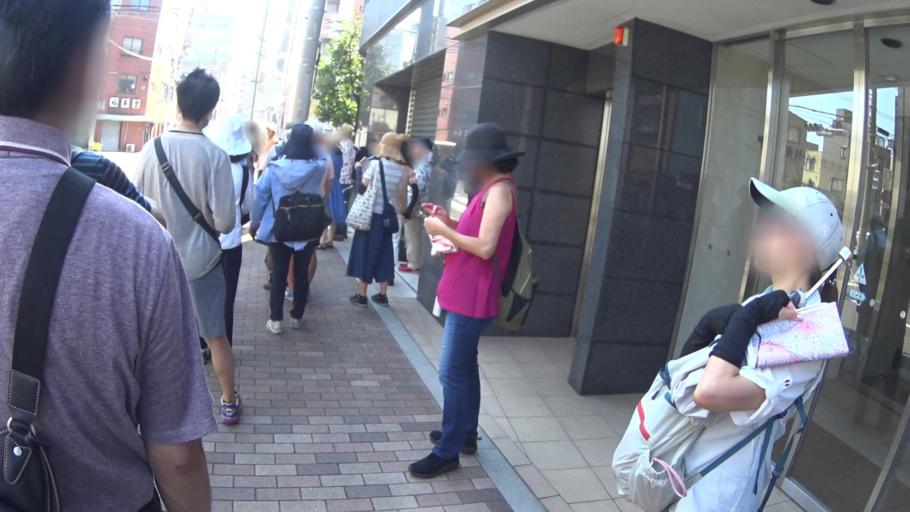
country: JP
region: Saitama
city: Soka
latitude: 35.7277
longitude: 139.7950
